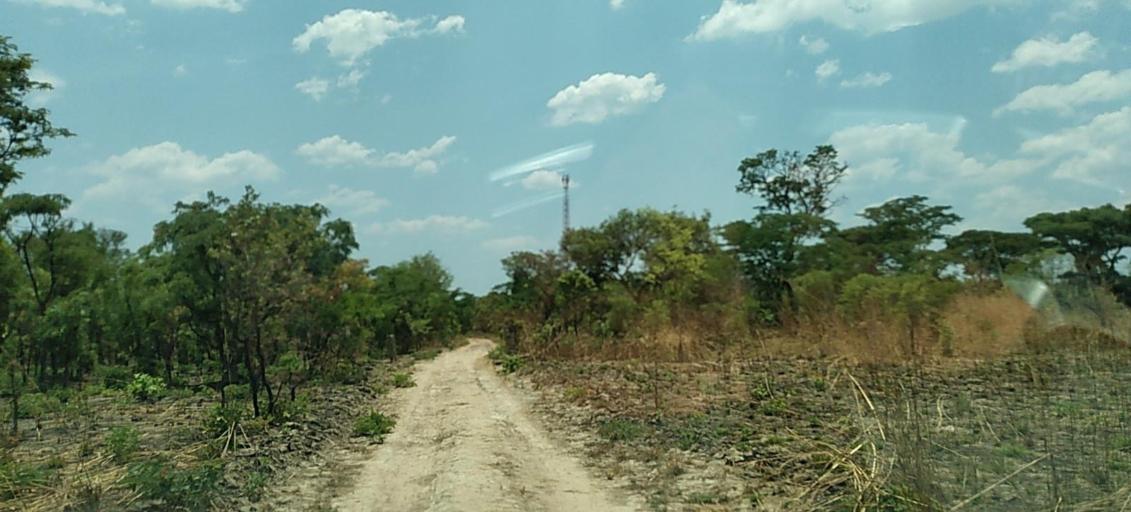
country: ZM
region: Copperbelt
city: Chililabombwe
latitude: -12.4508
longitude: 27.6785
